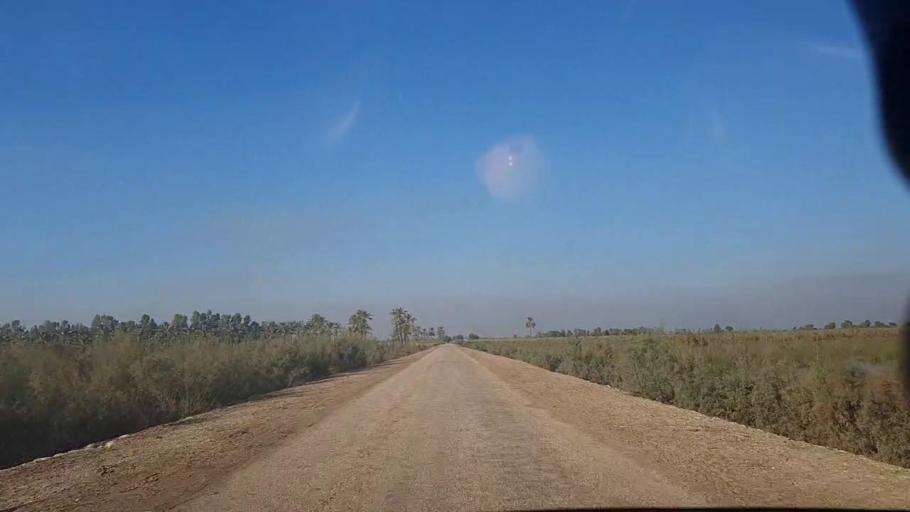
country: PK
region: Sindh
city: Sobhadero
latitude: 27.4064
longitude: 68.4221
